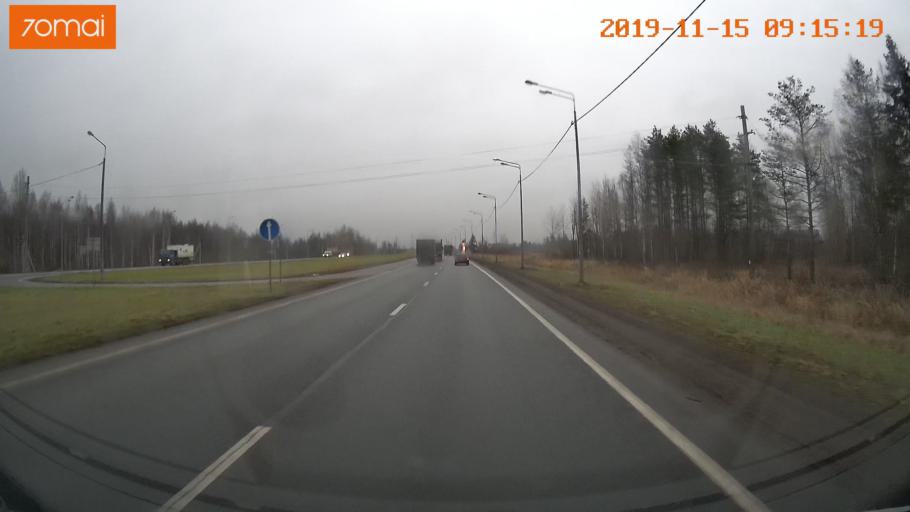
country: RU
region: Vologda
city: Tonshalovo
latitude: 59.2374
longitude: 37.9662
